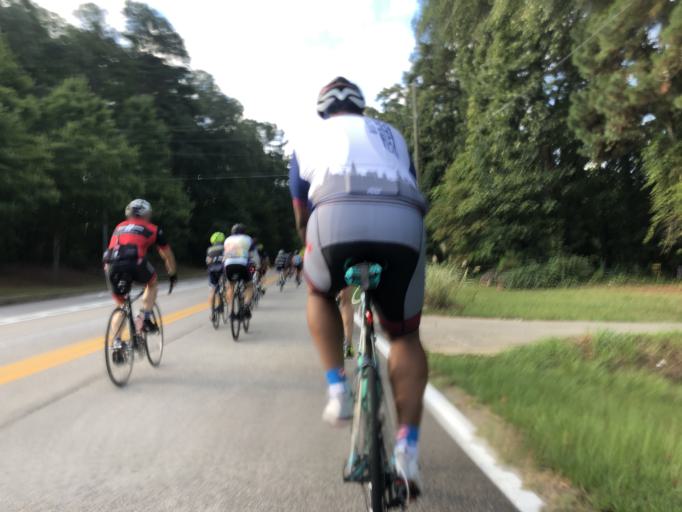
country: US
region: Georgia
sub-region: Fulton County
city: Palmetto
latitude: 33.5791
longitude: -84.6494
